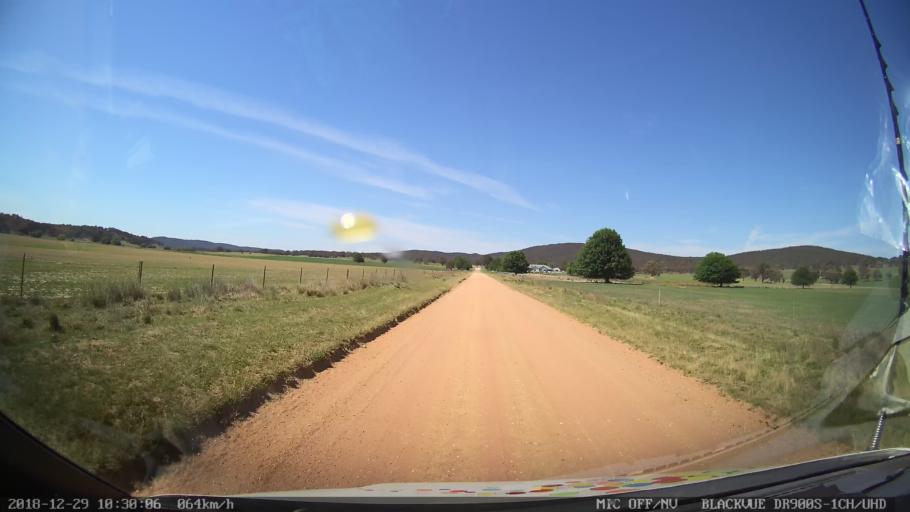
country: AU
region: New South Wales
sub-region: Yass Valley
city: Gundaroo
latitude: -34.9571
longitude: 149.4552
